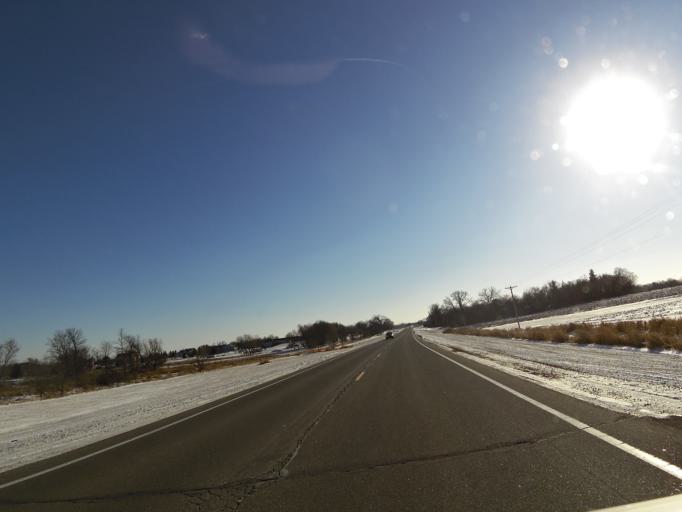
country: US
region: Minnesota
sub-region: Scott County
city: Prior Lake
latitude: 44.6690
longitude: -93.5009
